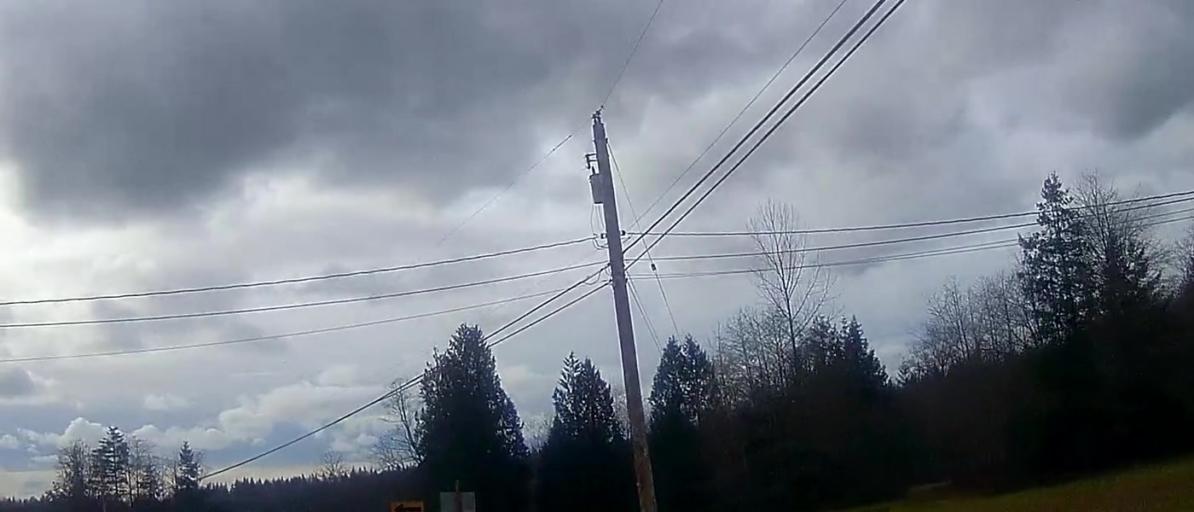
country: US
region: Washington
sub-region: Skagit County
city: Sedro-Woolley
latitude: 48.5790
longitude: -122.2956
